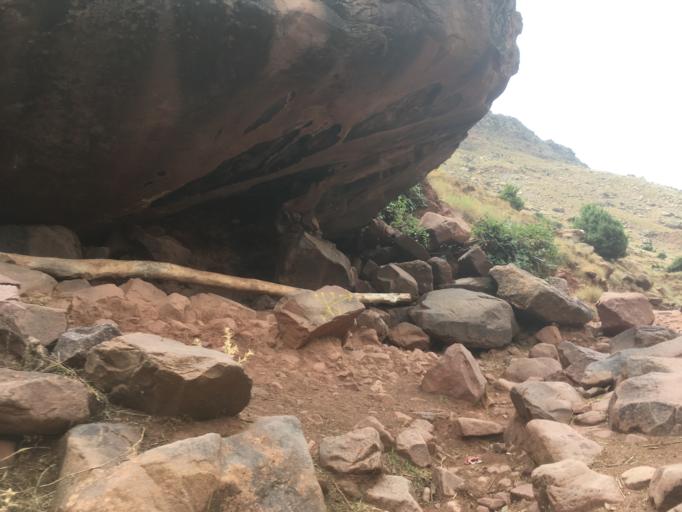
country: MA
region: Marrakech-Tensift-Al Haouz
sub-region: Al-Haouz
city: Tidili Mesfioua
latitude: 31.2954
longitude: -7.6689
